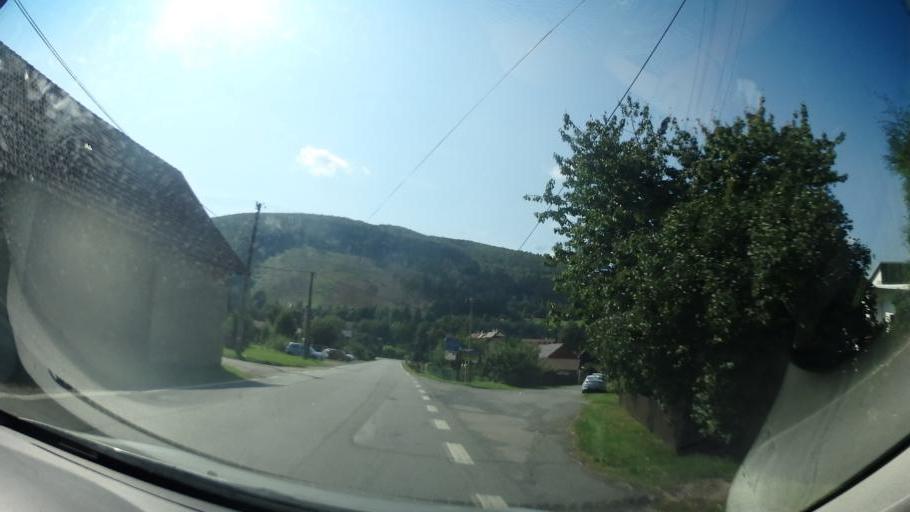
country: CZ
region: Pardubicky
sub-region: Okres Svitavy
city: Bystre
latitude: 49.5555
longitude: 16.3316
